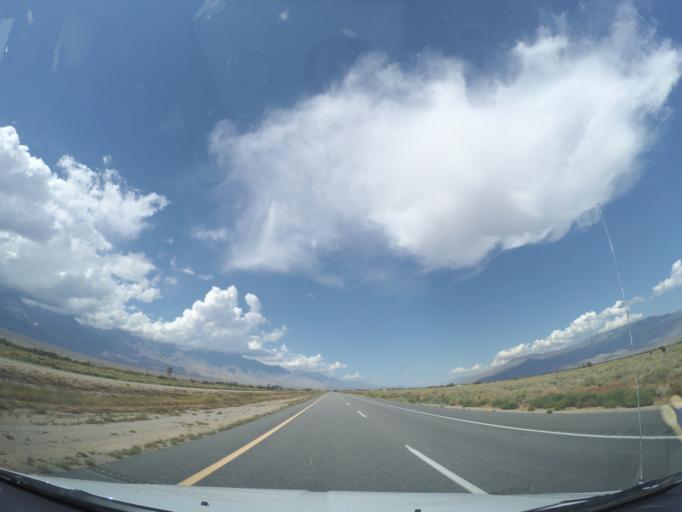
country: US
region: California
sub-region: Inyo County
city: Lone Pine
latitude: 36.7301
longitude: -118.1457
